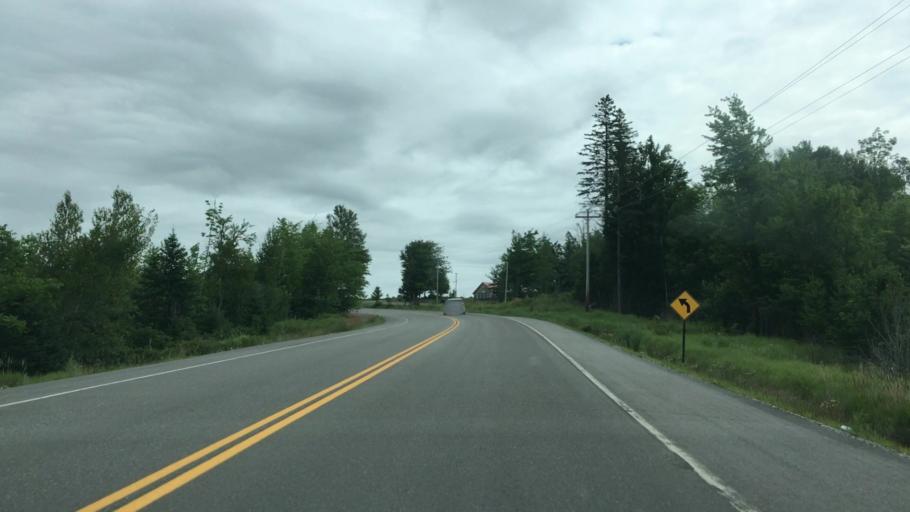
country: US
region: Maine
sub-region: Washington County
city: Machias
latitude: 45.0005
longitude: -67.5560
